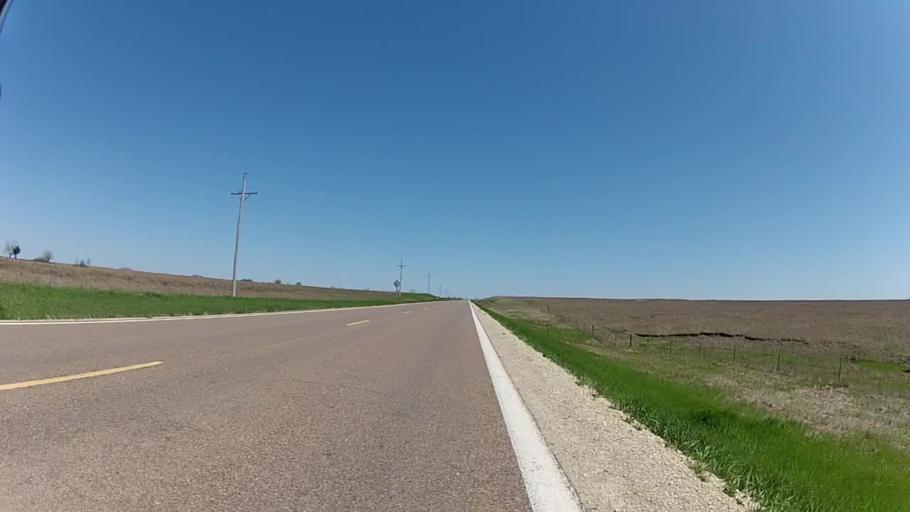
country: US
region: Kansas
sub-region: Wabaunsee County
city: Alma
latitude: 38.9352
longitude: -96.5202
